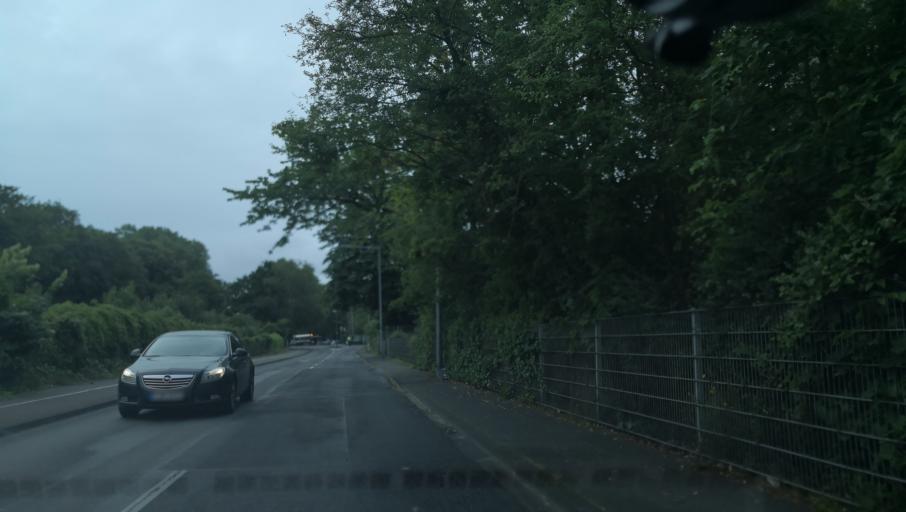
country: DE
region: North Rhine-Westphalia
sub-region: Regierungsbezirk Koln
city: Mengenich
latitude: 50.9699
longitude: 6.8923
